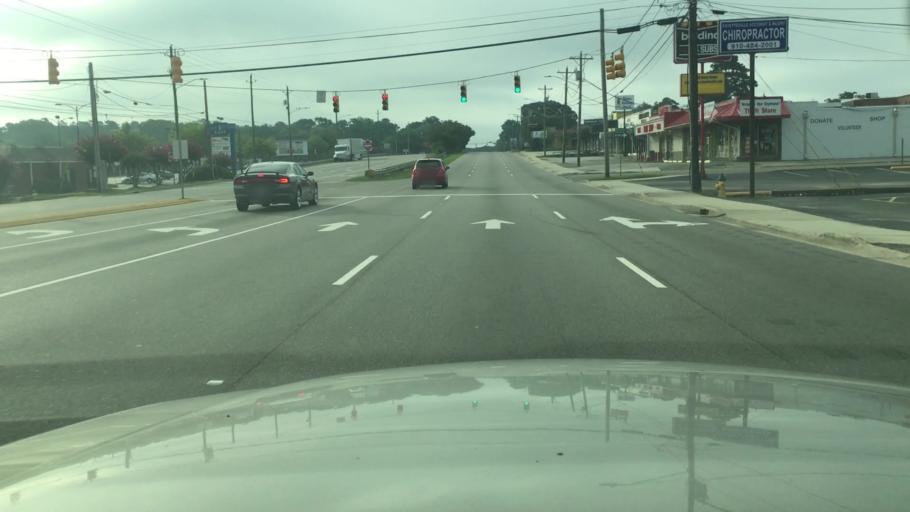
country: US
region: North Carolina
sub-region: Cumberland County
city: Fayetteville
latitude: 35.0737
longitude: -78.9273
